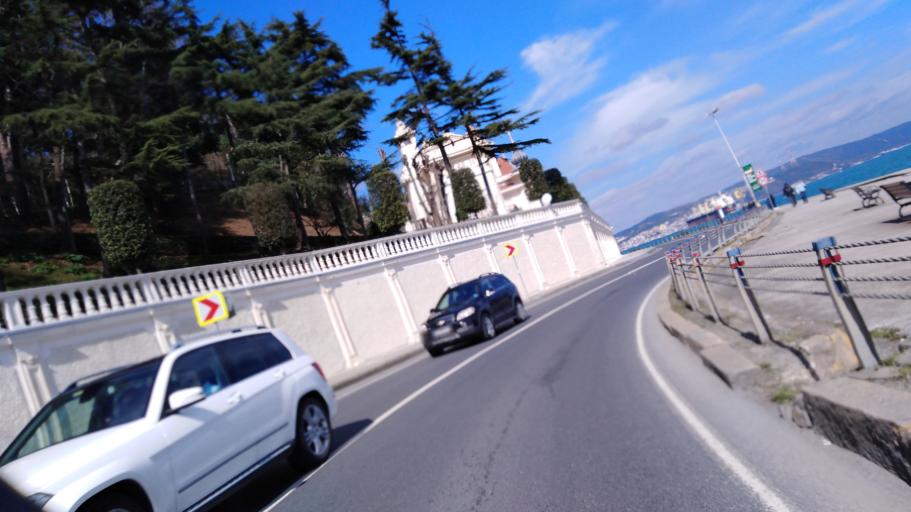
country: TR
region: Istanbul
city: Sisli
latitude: 41.1334
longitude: 29.0625
